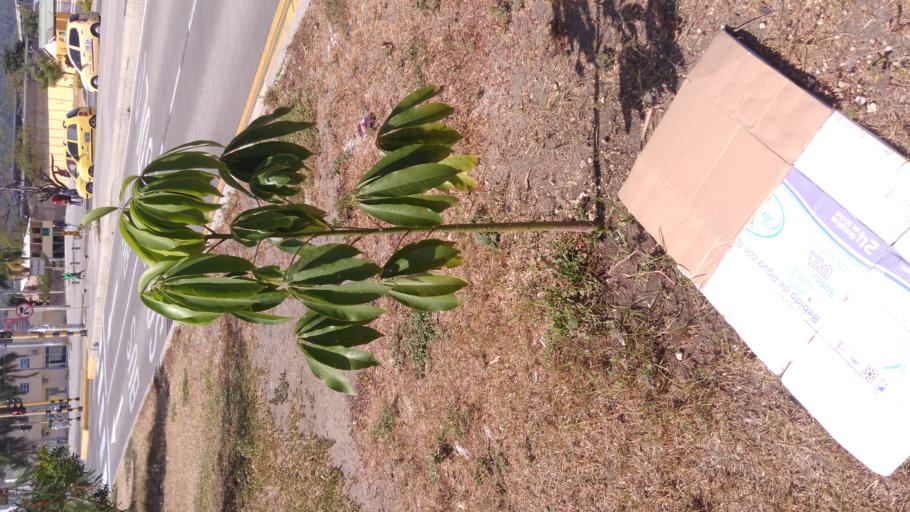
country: CO
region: Bolivar
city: Cartagena
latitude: 10.4087
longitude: -75.5150
